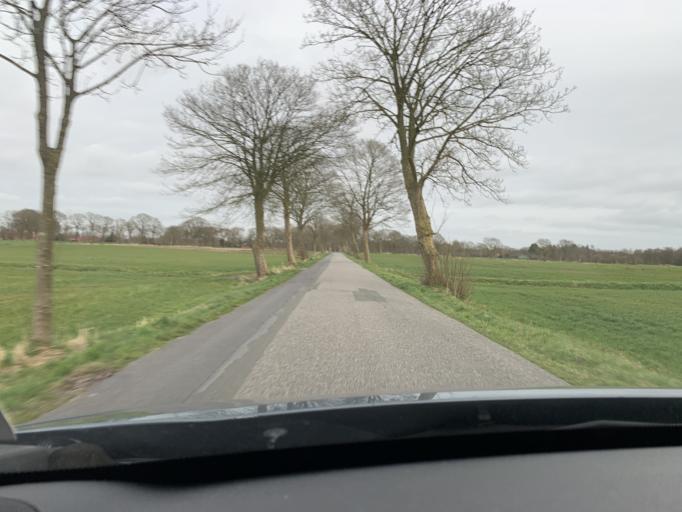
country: DE
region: Lower Saxony
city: Schwerinsdorf
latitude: 53.2690
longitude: 7.7020
